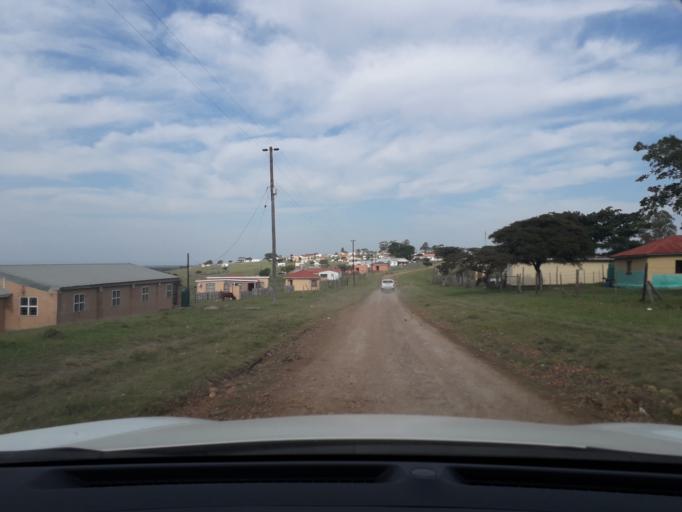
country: ZA
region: Eastern Cape
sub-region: Buffalo City Metropolitan Municipality
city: Bhisho
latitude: -32.9849
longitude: 27.3614
